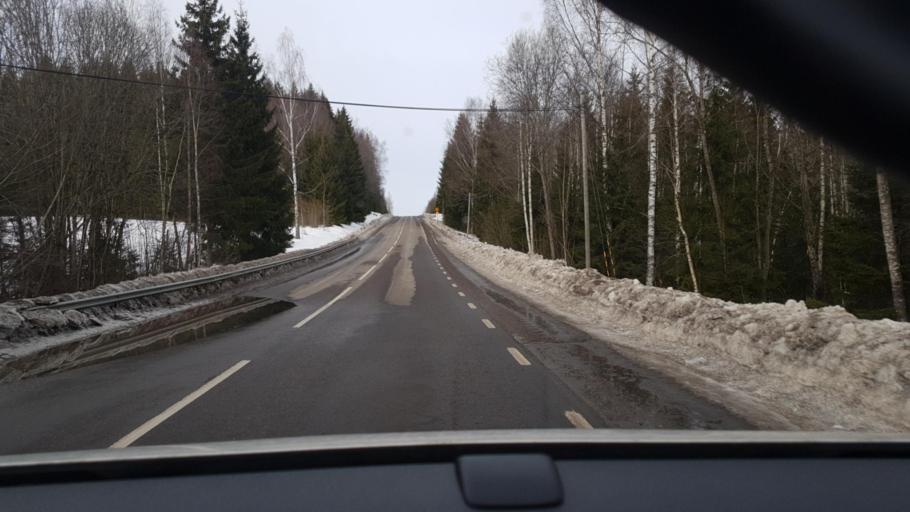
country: SE
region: Vaermland
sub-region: Eda Kommun
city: Amotfors
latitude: 59.7387
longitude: 12.3827
